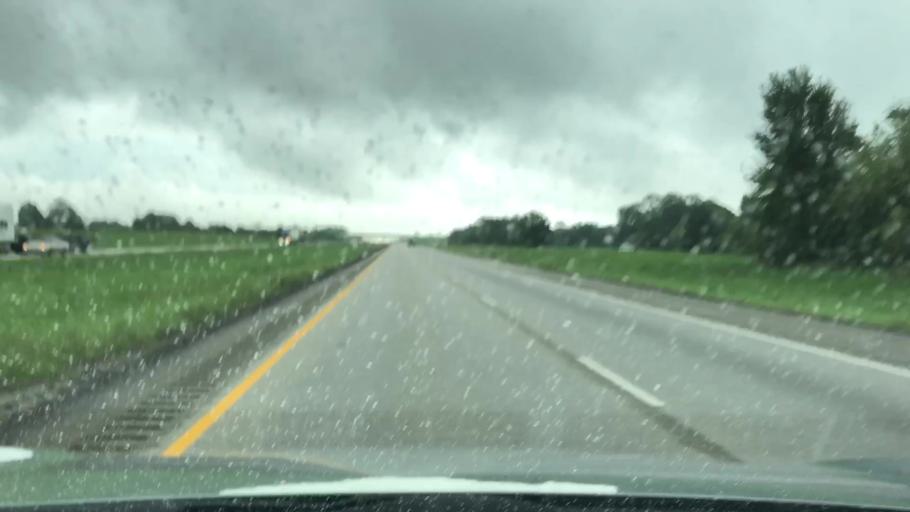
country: US
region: Texas
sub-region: Fayette County
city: Flatonia
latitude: 29.6965
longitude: -97.1370
